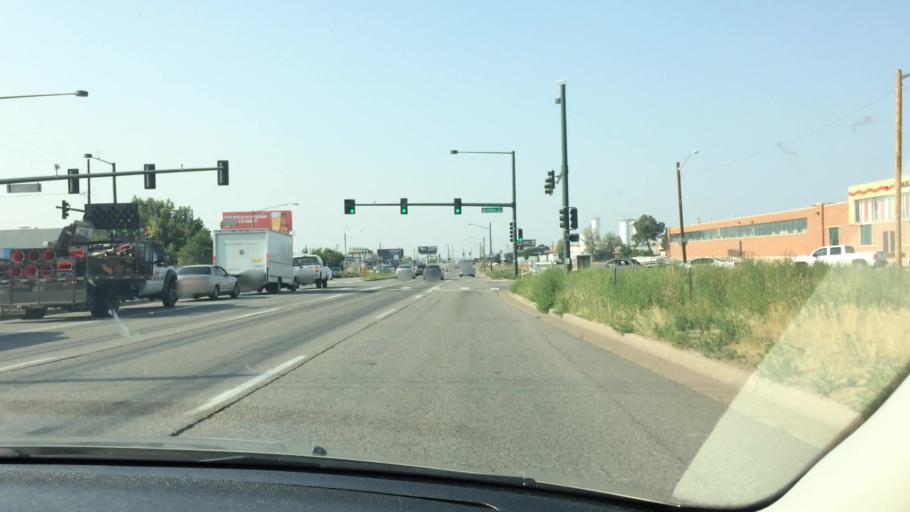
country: US
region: Colorado
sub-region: Adams County
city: Commerce City
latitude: 39.7833
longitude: -104.9404
